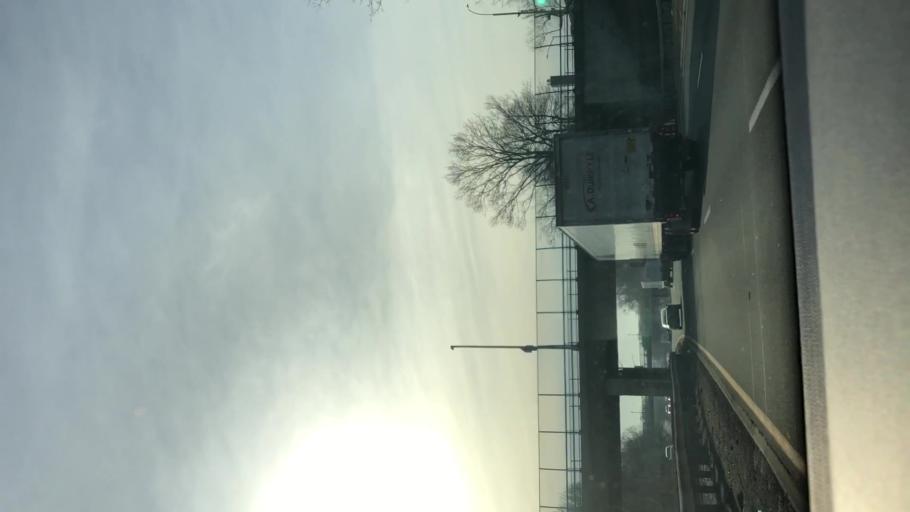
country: US
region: New York
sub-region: Nassau County
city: East Atlantic Beach
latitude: 40.7718
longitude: -73.7839
